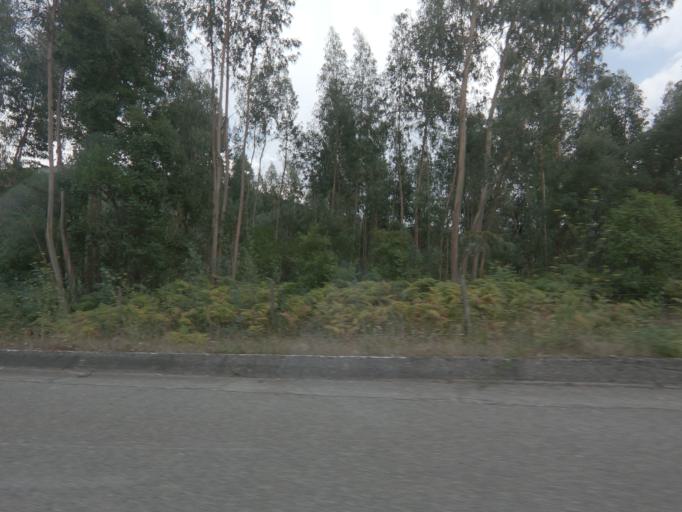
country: PT
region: Coimbra
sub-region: Penacova
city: Penacova
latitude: 40.2804
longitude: -8.2708
